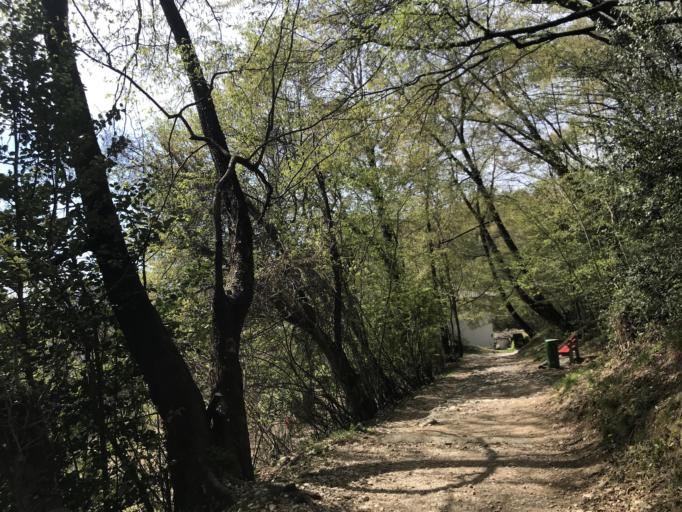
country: CH
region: Ticino
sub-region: Lugano District
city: Melide
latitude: 45.9692
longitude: 8.9409
